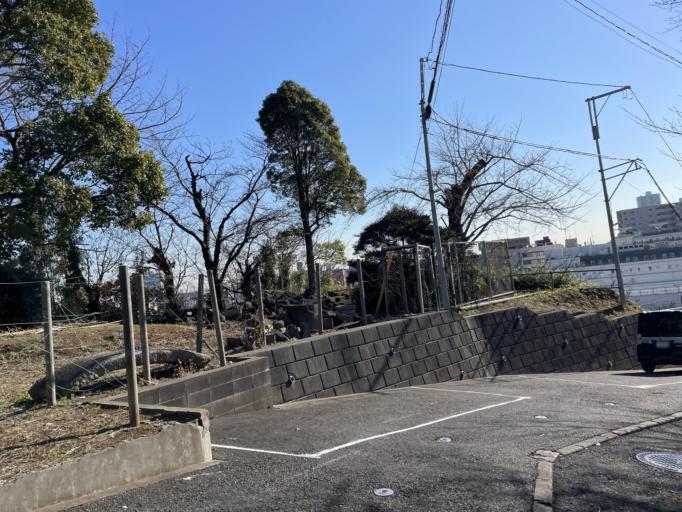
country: JP
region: Kanagawa
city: Yokohama
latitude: 35.4827
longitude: 139.6332
